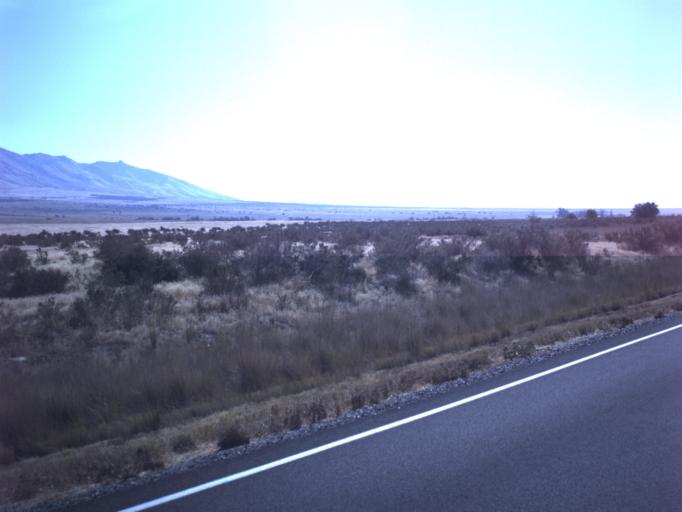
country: US
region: Utah
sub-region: Tooele County
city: Grantsville
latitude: 40.4743
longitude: -112.7461
